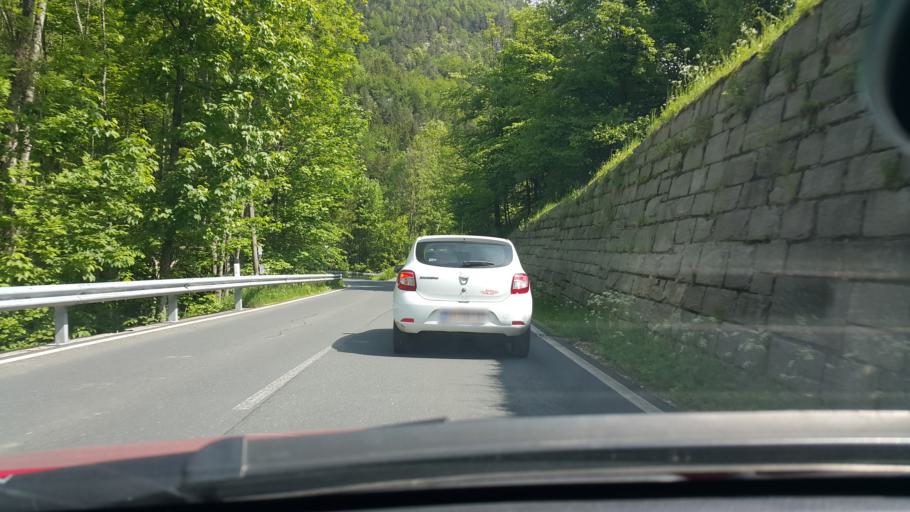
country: AT
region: Carinthia
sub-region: Politischer Bezirk Klagenfurt Land
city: Ferlach
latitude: 46.4793
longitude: 14.2562
